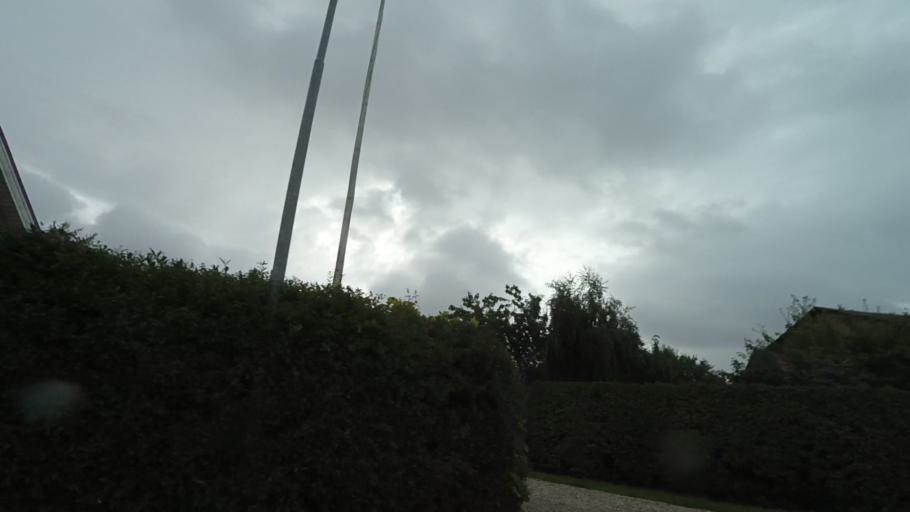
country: DK
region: Central Jutland
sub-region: Syddjurs Kommune
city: Ronde
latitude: 56.3132
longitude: 10.4618
